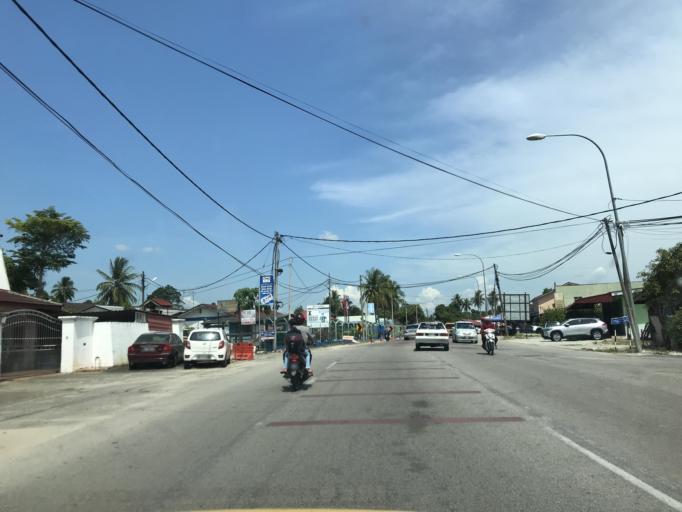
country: MY
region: Kelantan
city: Kota Bharu
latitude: 6.1182
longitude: 102.1947
